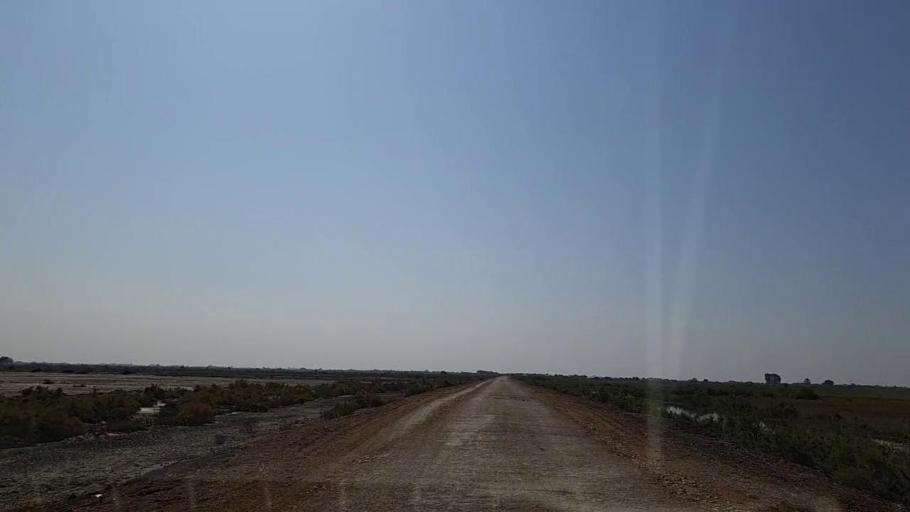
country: PK
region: Sindh
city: Chuhar Jamali
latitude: 24.4808
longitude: 68.0917
